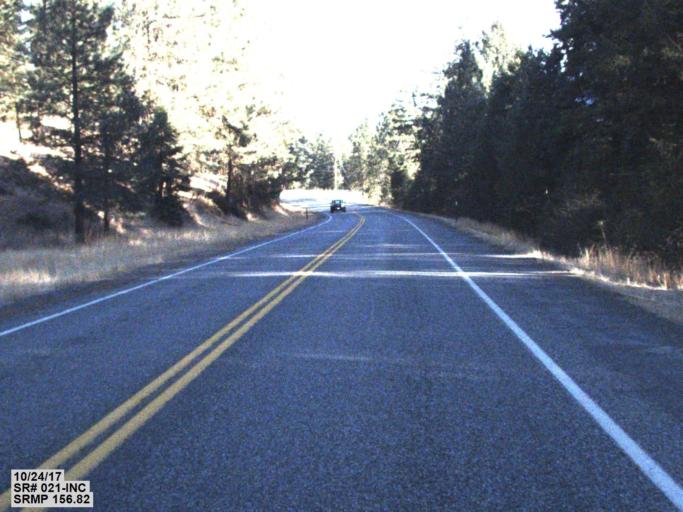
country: US
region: Washington
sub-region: Ferry County
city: Republic
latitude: 48.5956
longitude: -118.7399
